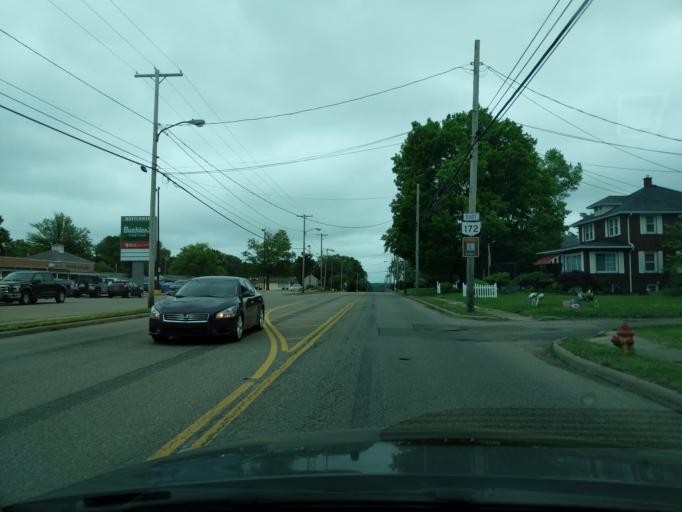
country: US
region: Ohio
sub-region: Stark County
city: Massillon
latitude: 40.7952
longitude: -81.5507
